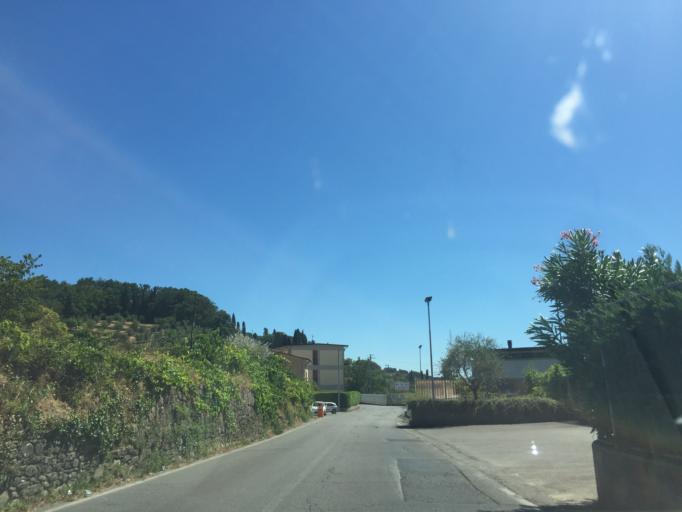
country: IT
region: Tuscany
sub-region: Provincia di Pistoia
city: Pistoia
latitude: 43.9756
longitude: 10.8902
